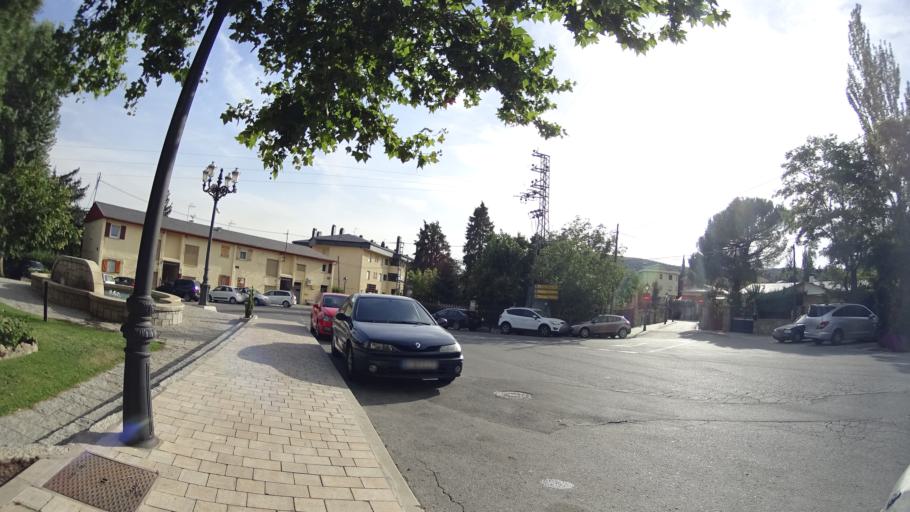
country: ES
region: Madrid
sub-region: Provincia de Madrid
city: Navacerrada
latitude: 40.7305
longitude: -4.0106
